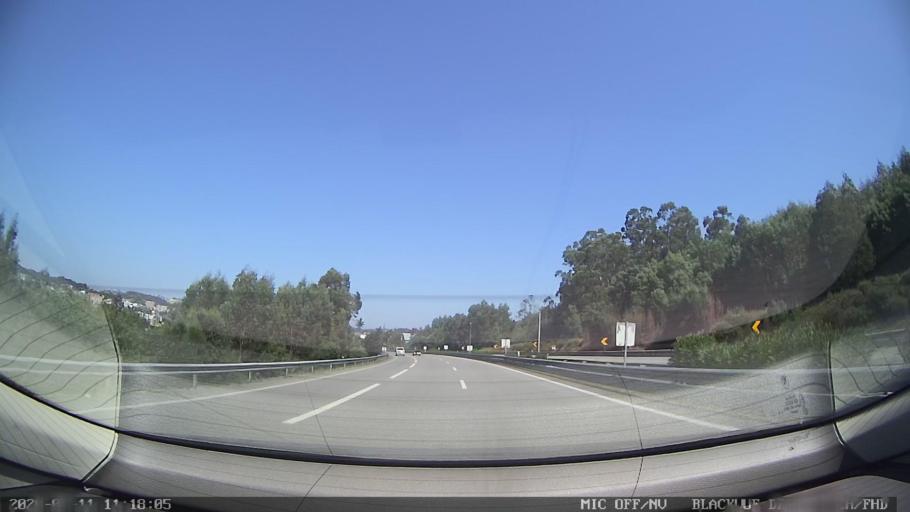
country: PT
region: Porto
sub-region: Valongo
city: Campo
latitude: 41.1960
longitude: -8.4848
